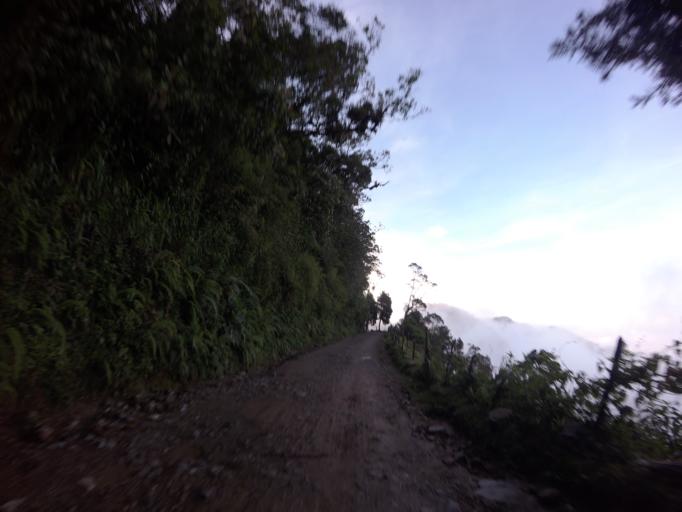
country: CO
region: Caldas
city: Pensilvania
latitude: 5.4308
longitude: -75.1312
